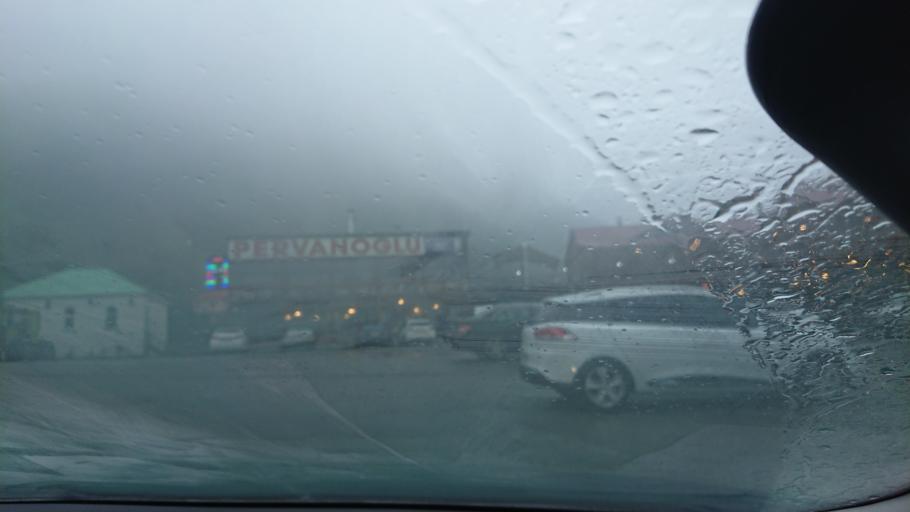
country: TR
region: Gumushane
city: Yaglidere
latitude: 40.6745
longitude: 39.4201
